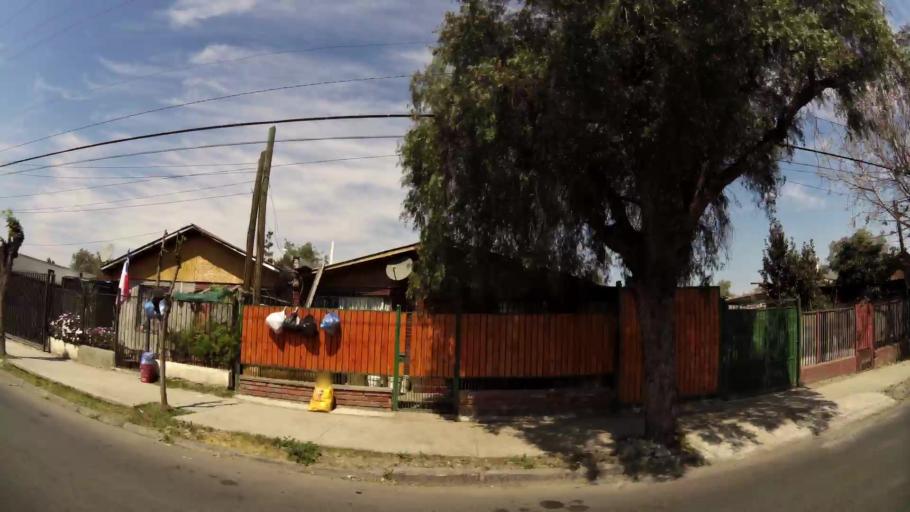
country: CL
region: Santiago Metropolitan
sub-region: Provincia de Santiago
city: La Pintana
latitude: -33.5533
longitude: -70.6384
